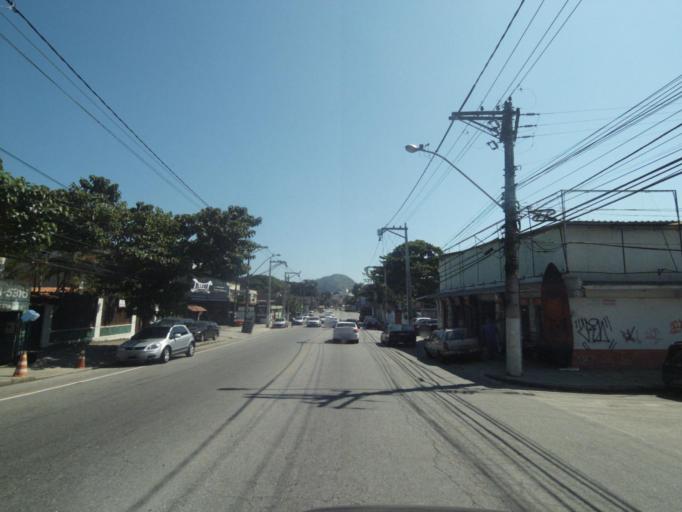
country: BR
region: Rio de Janeiro
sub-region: Niteroi
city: Niteroi
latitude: -22.9049
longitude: -43.0518
